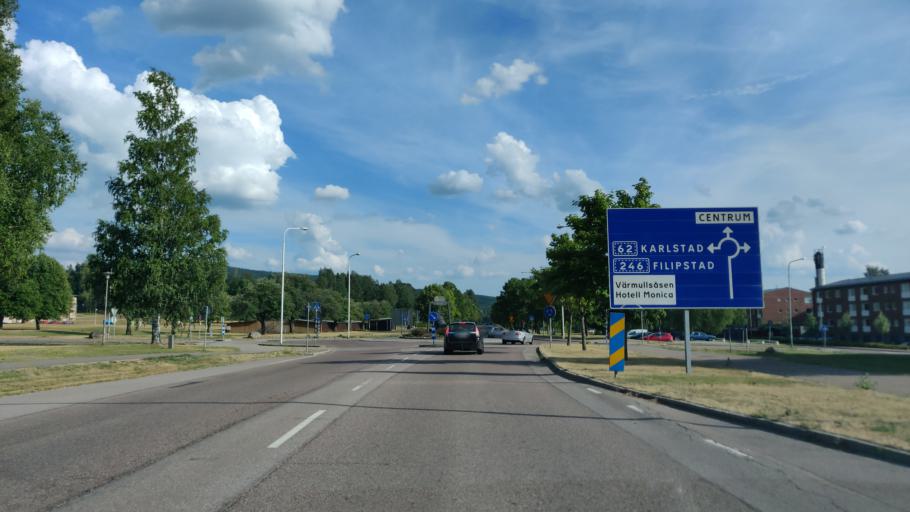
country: SE
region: Vaermland
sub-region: Hagfors Kommun
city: Hagfors
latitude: 60.0411
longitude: 13.6898
